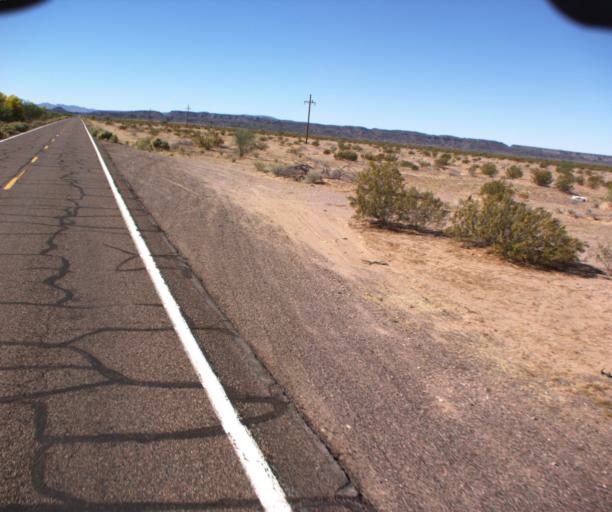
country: US
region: Arizona
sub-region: Pima County
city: Ajo
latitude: 32.6152
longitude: -112.8677
